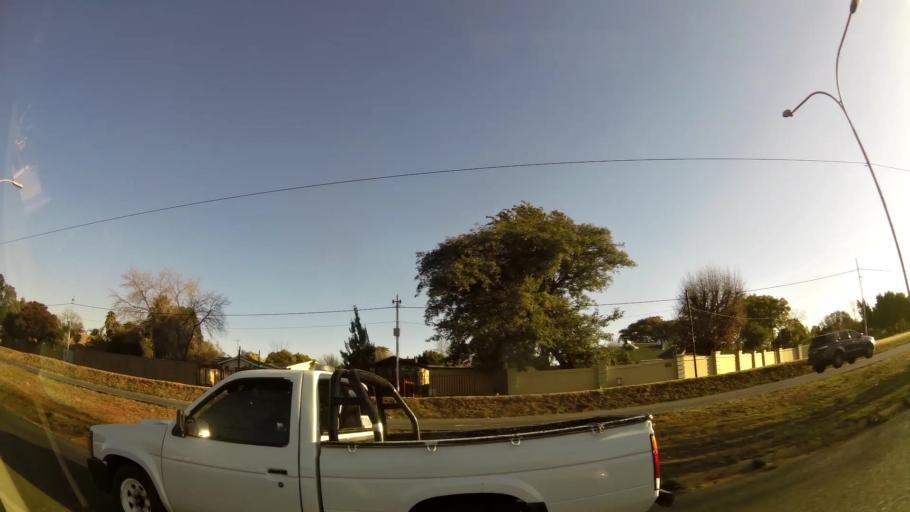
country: ZA
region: Gauteng
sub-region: City of Johannesburg Metropolitan Municipality
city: Roodepoort
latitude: -26.1592
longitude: 27.9179
